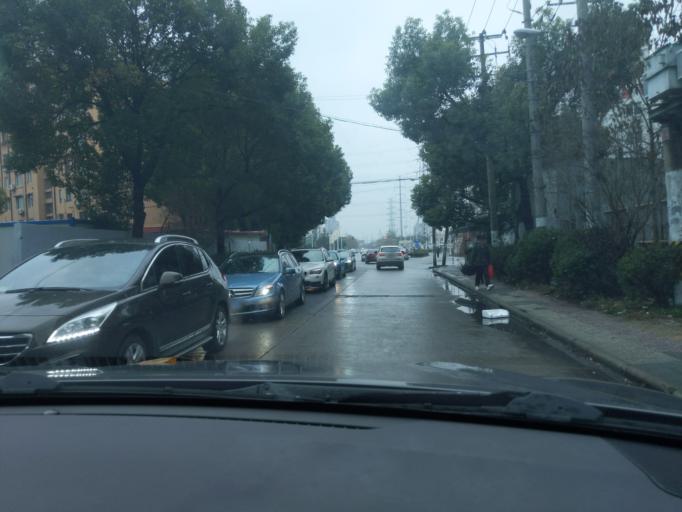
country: CN
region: Shanghai Shi
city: Huamu
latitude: 31.1891
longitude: 121.5248
